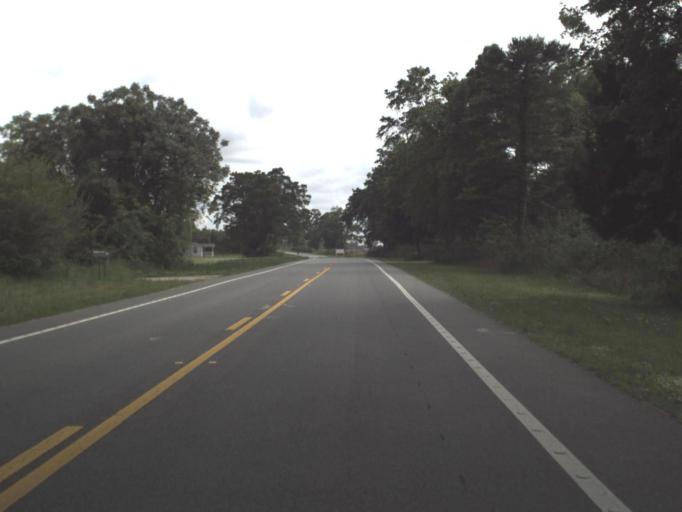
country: US
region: Alabama
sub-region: Escambia County
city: East Brewton
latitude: 30.9827
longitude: -87.0430
